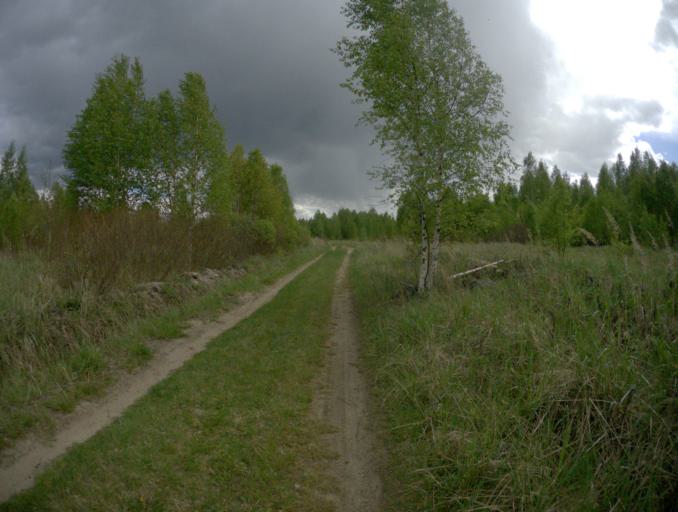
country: RU
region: Vladimir
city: Urshel'skiy
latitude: 55.6049
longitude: 40.1602
